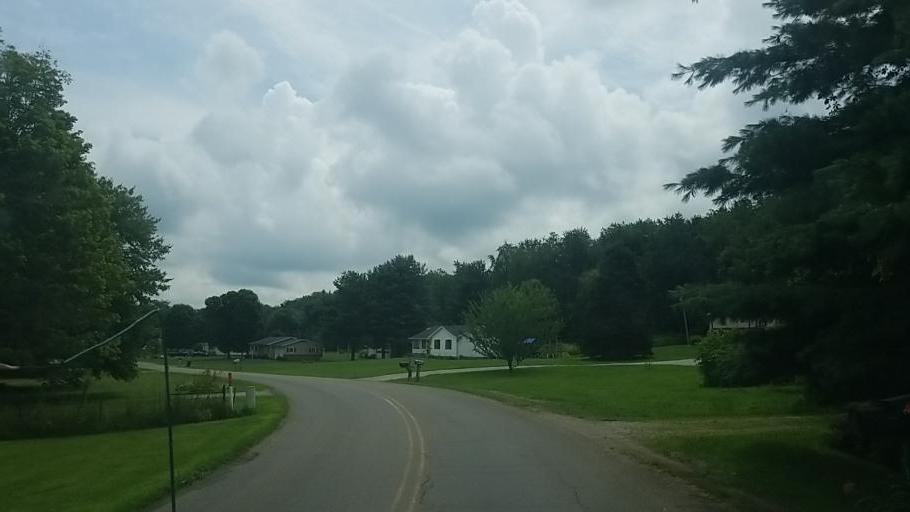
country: US
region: Ohio
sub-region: Knox County
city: Gambier
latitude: 40.3955
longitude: -82.3648
